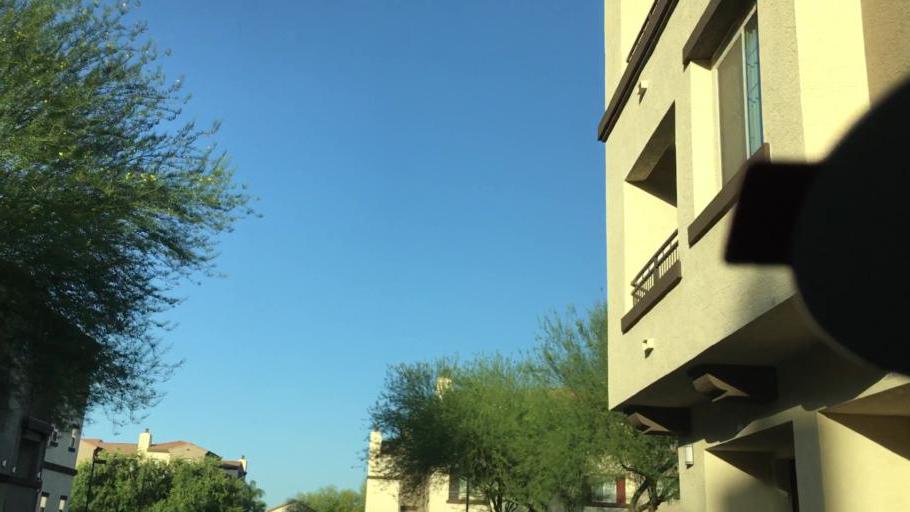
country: US
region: Arizona
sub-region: Maricopa County
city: Peoria
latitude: 33.6129
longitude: -112.2347
